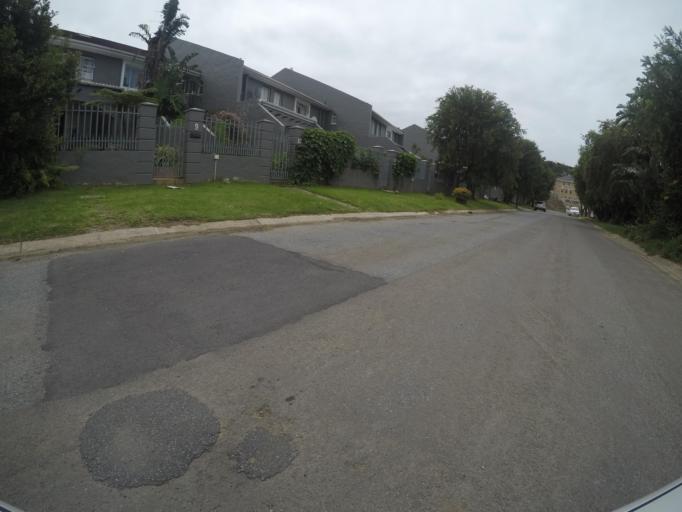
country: ZA
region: Eastern Cape
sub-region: Buffalo City Metropolitan Municipality
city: East London
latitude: -32.9815
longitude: 27.9385
